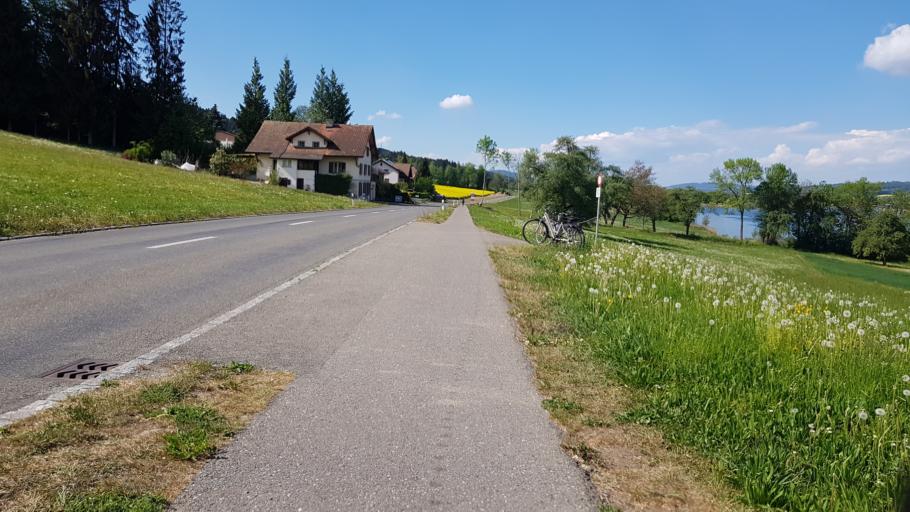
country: CH
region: Lucerne
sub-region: Hochdorf District
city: Hitzkirch
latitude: 47.2018
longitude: 8.2470
